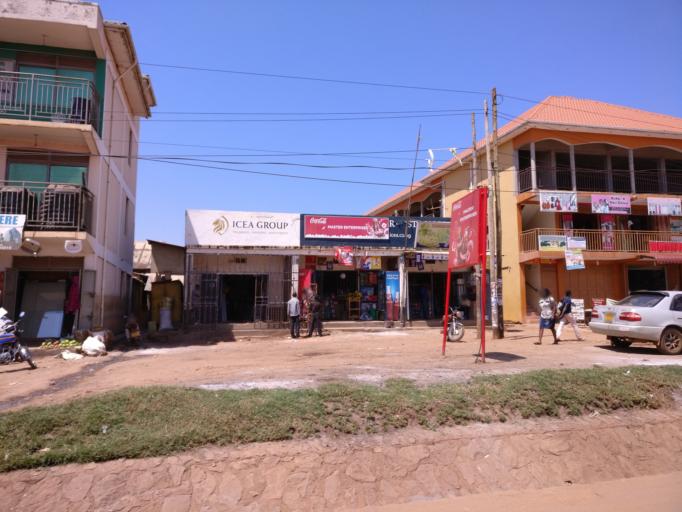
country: UG
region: Central Region
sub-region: Wakiso District
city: Entebbe
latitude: 0.0933
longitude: 32.5002
